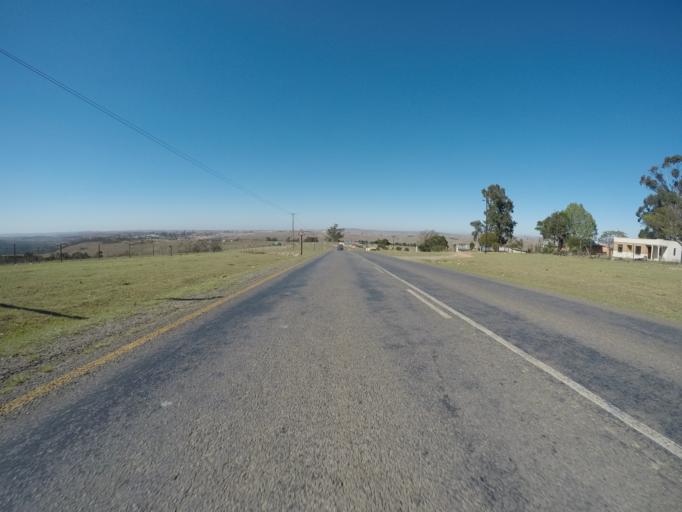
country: ZA
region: Eastern Cape
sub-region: OR Tambo District Municipality
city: Mthatha
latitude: -31.7931
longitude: 28.7451
